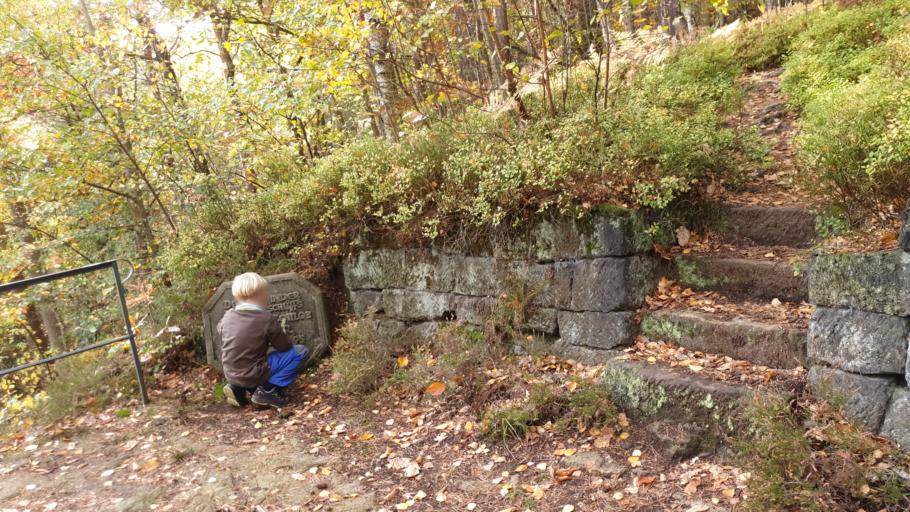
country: DE
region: Saxony
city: Bad Schandau
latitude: 50.9071
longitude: 14.1639
